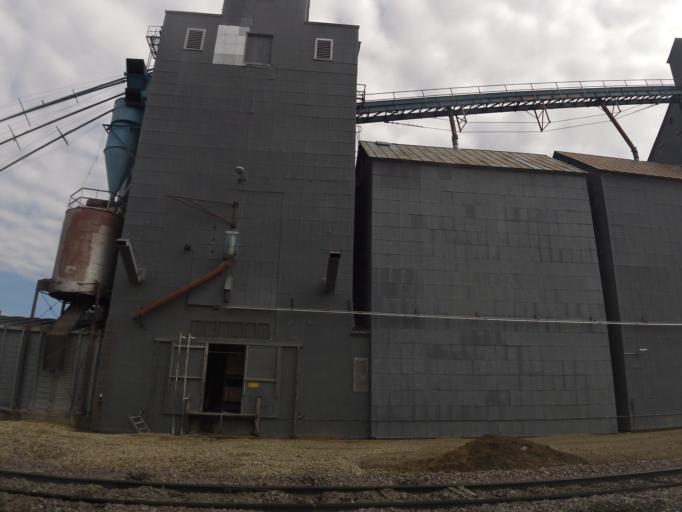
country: US
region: North Dakota
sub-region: Walsh County
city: Grafton
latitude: 48.2932
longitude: -97.3698
